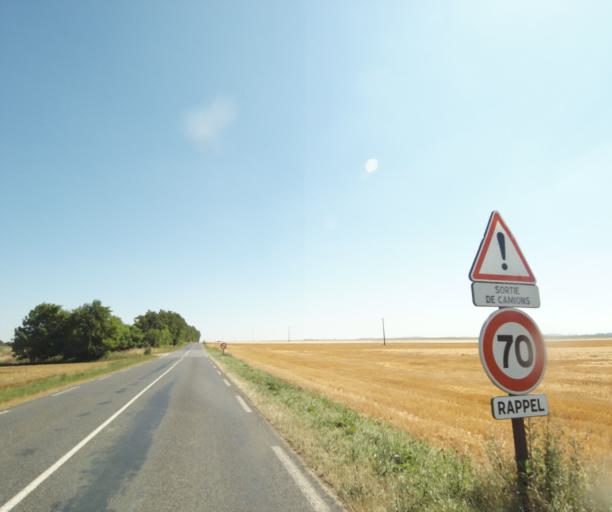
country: FR
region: Ile-de-France
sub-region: Departement de Seine-et-Marne
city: La Chapelle-la-Reine
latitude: 48.3029
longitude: 2.5735
